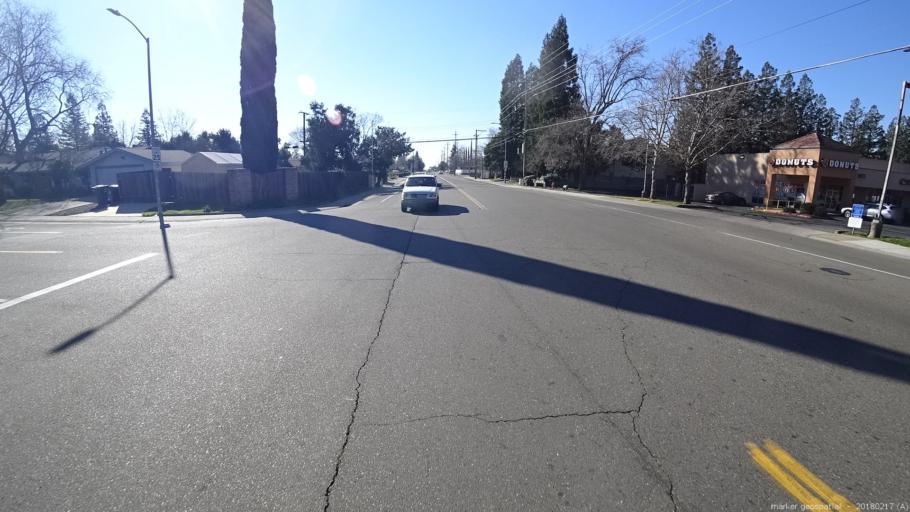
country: US
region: California
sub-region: Sacramento County
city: Orangevale
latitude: 38.6713
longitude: -121.2025
